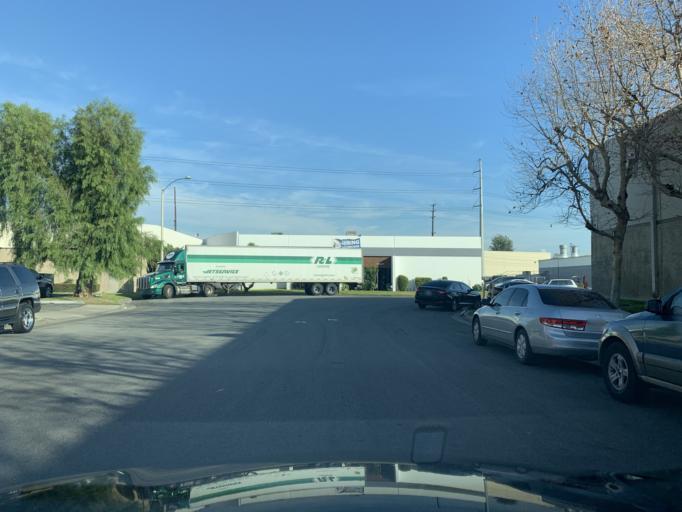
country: US
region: California
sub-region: Orange County
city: Anaheim
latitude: 33.8157
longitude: -117.9005
